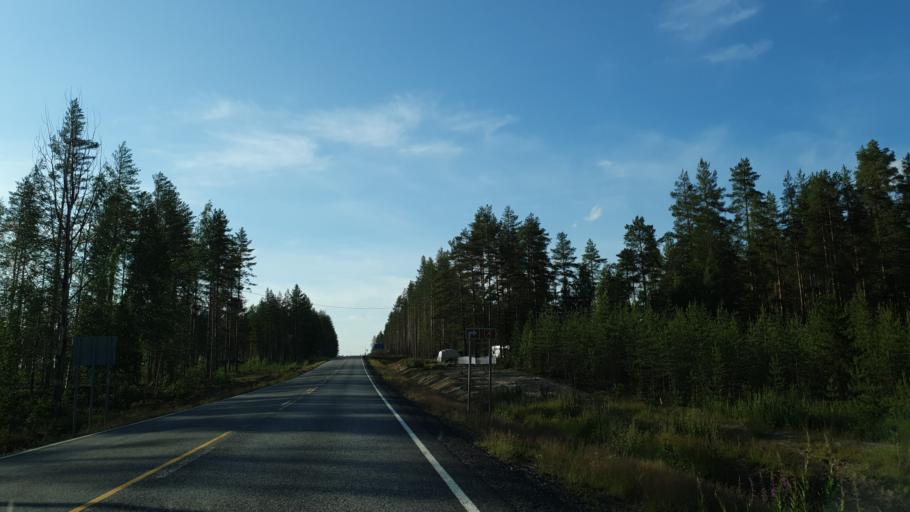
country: FI
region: Kainuu
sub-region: Kehys-Kainuu
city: Kuhmo
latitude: 64.0945
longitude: 29.4782
